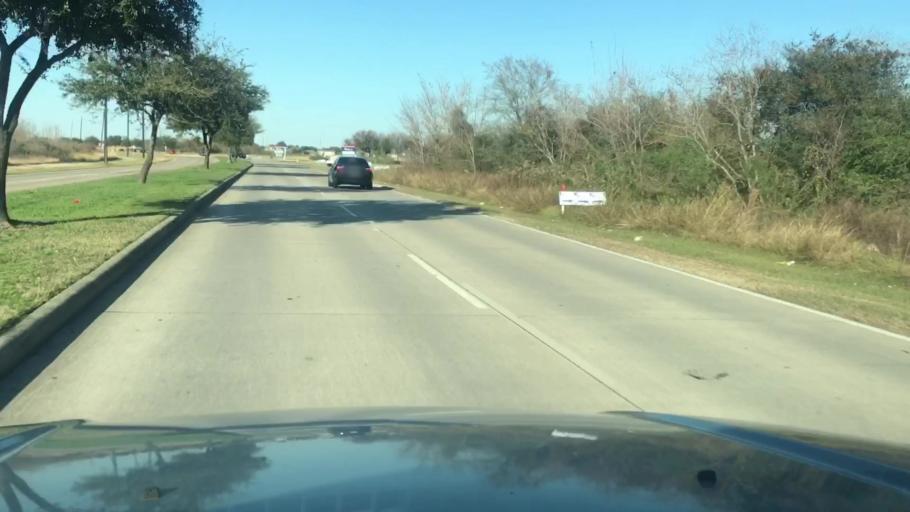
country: US
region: Texas
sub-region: Fort Bend County
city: Cinco Ranch
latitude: 29.8347
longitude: -95.7193
